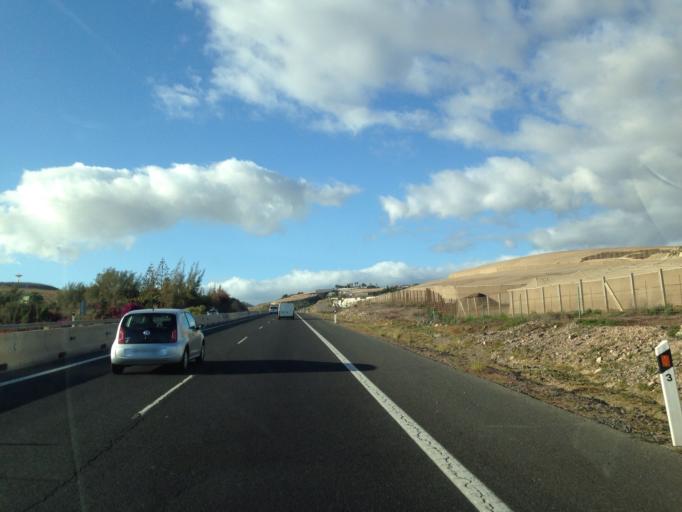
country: ES
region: Canary Islands
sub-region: Provincia de Las Palmas
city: Maspalomas
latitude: 27.7588
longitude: -15.6219
